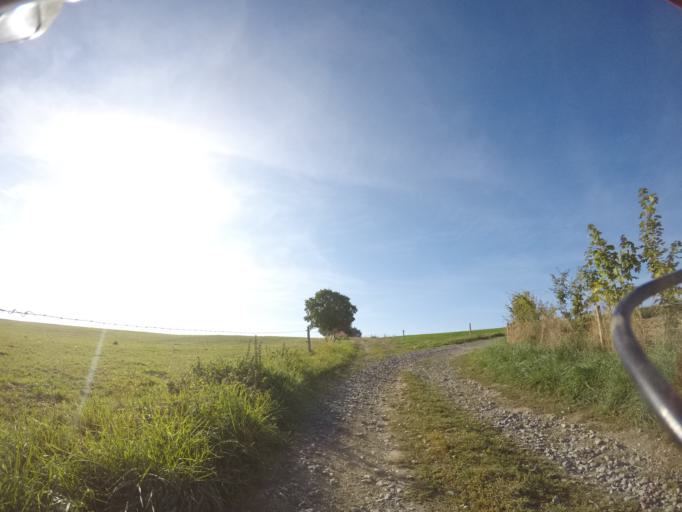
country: BE
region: Wallonia
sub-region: Province du Luxembourg
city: Fauvillers
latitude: 49.9136
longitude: 5.6597
